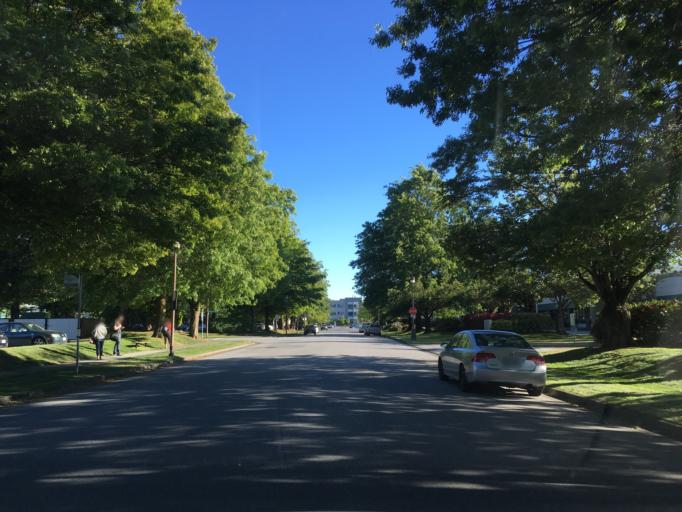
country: CA
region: British Columbia
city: Richmond
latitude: 49.1743
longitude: -123.0717
